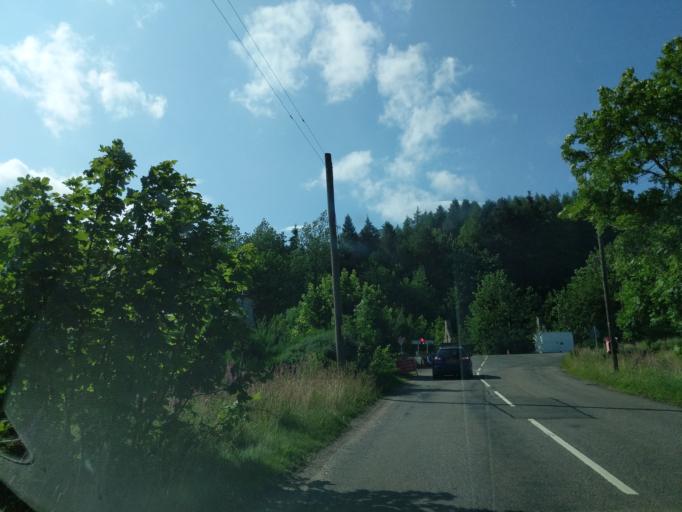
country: GB
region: Scotland
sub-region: Moray
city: Rothes
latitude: 57.5539
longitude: -3.1524
